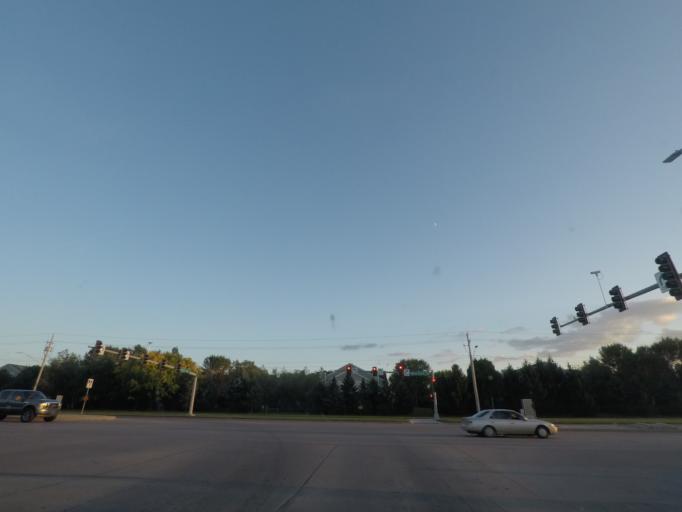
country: US
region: Iowa
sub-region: Polk County
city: Clive
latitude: 41.5594
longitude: -93.7855
